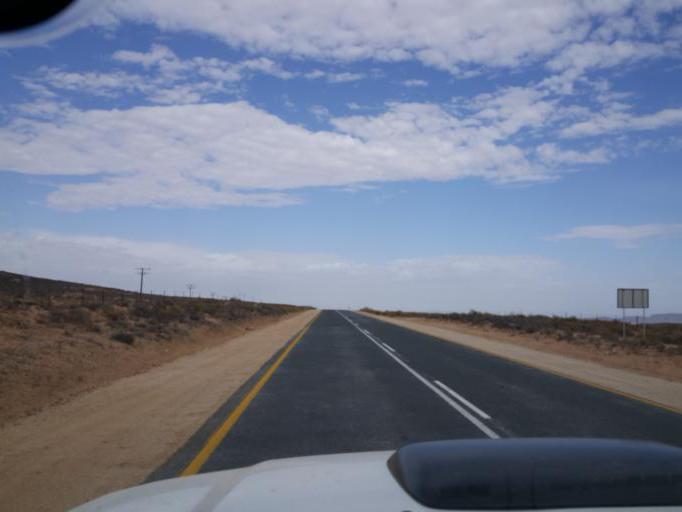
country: ZA
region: Northern Cape
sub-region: Namakwa District Municipality
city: Springbok
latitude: -29.2276
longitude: 17.6762
